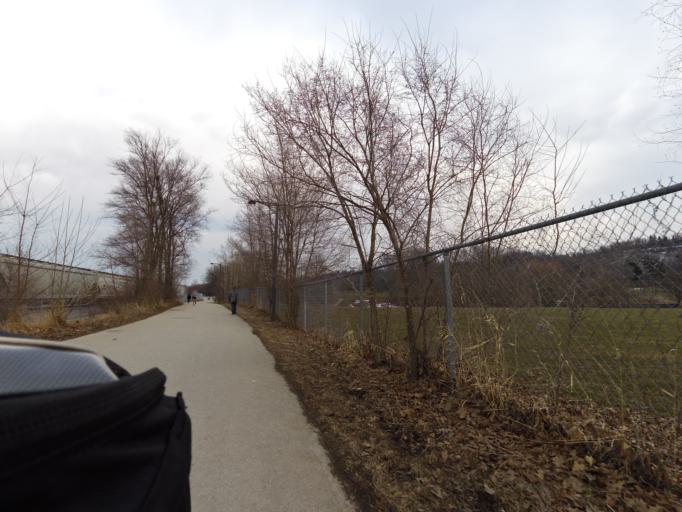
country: CA
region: Ontario
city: Hamilton
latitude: 43.2521
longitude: -79.9118
